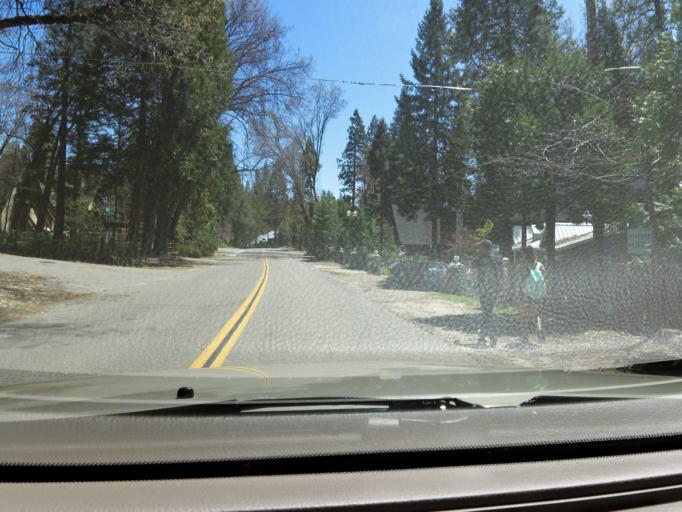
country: US
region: California
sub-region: Madera County
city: Oakhurst
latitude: 37.3256
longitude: -119.5696
